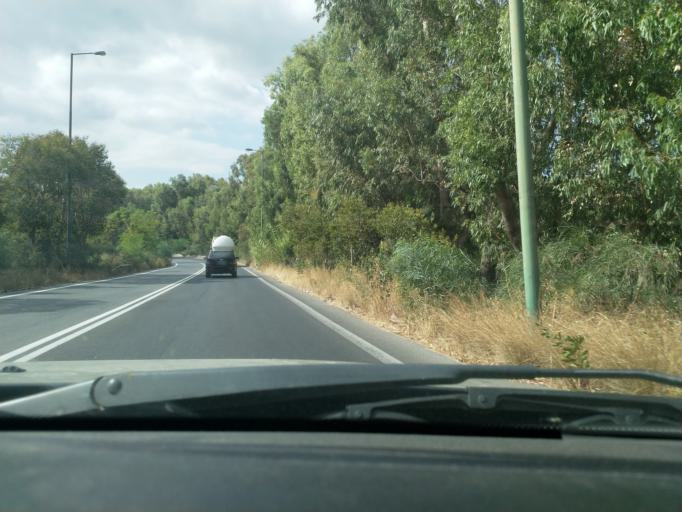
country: GR
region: Crete
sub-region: Nomos Chanias
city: Georgioupolis
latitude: 35.3611
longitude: 24.2578
